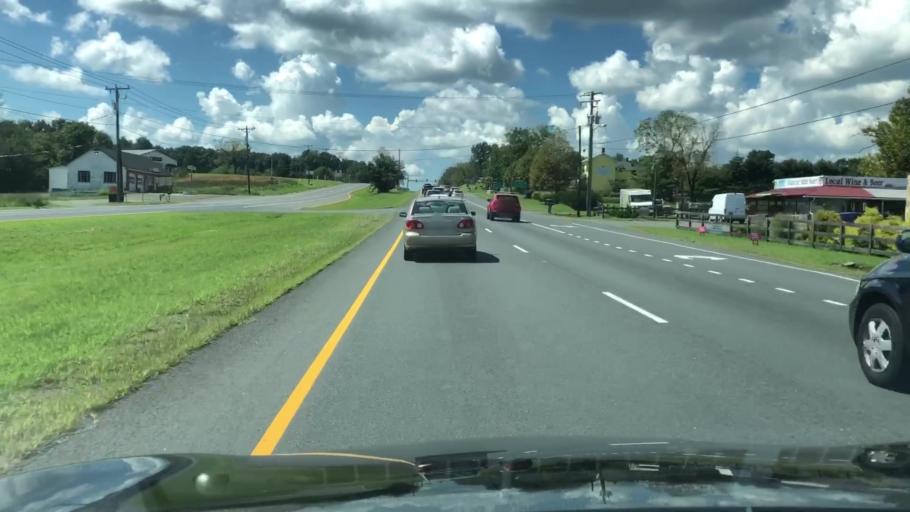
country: US
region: Virginia
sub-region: Fauquier County
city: New Baltimore
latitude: 38.7792
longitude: -77.6790
